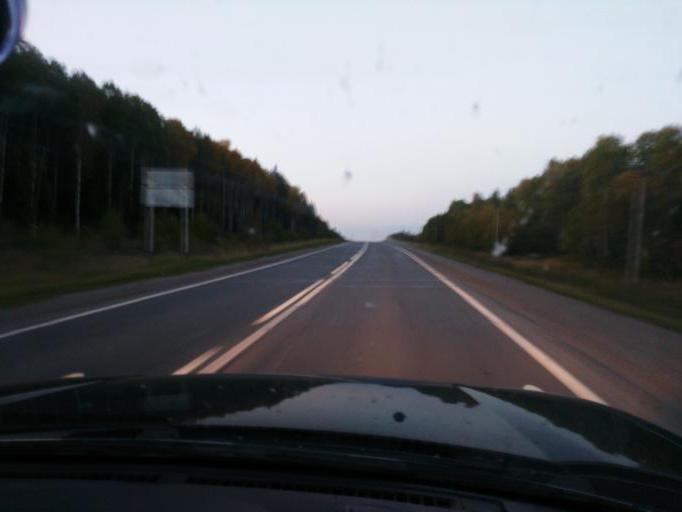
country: RU
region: Perm
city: Verkhnechusovskiye Gorodki
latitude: 58.2284
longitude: 57.2061
